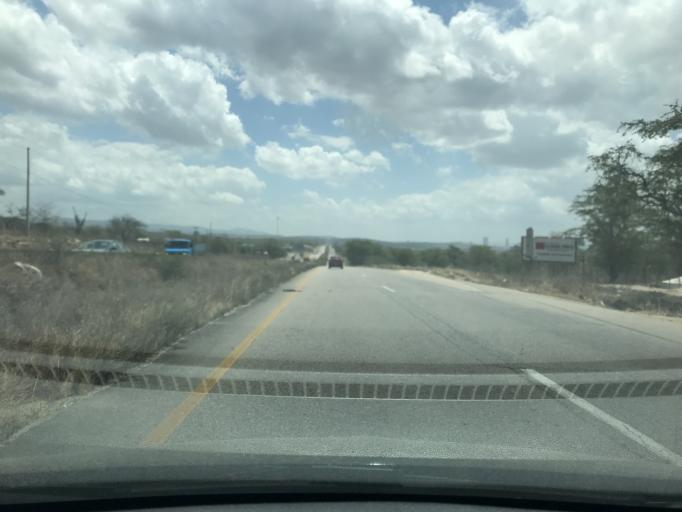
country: BR
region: Pernambuco
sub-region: Caruaru
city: Caruaru
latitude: -8.2962
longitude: -35.8927
